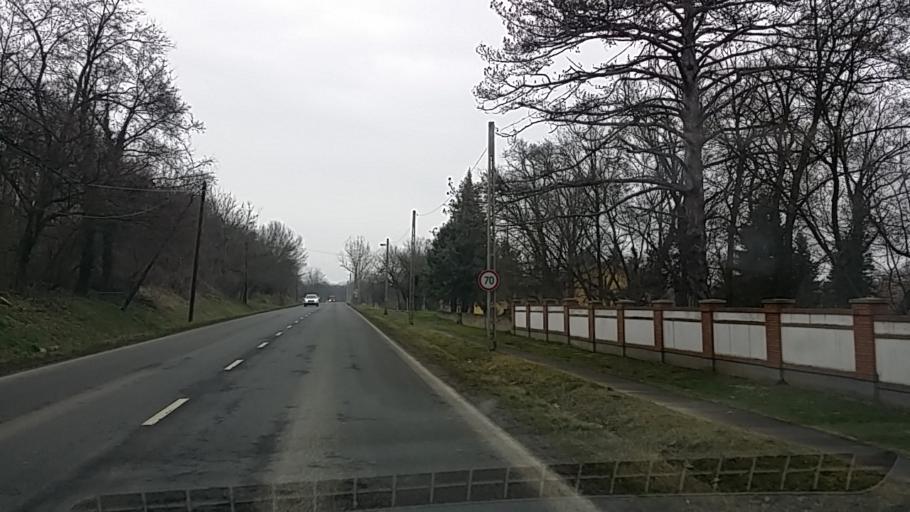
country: HU
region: Baranya
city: Dunaszekcso
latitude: 46.0560
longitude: 18.7242
